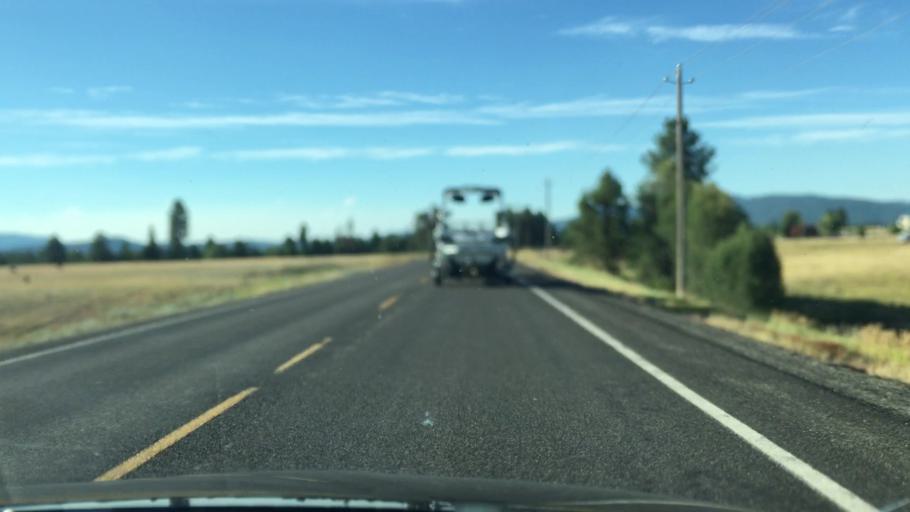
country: US
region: Idaho
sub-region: Valley County
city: Cascade
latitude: 44.4504
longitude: -115.9994
